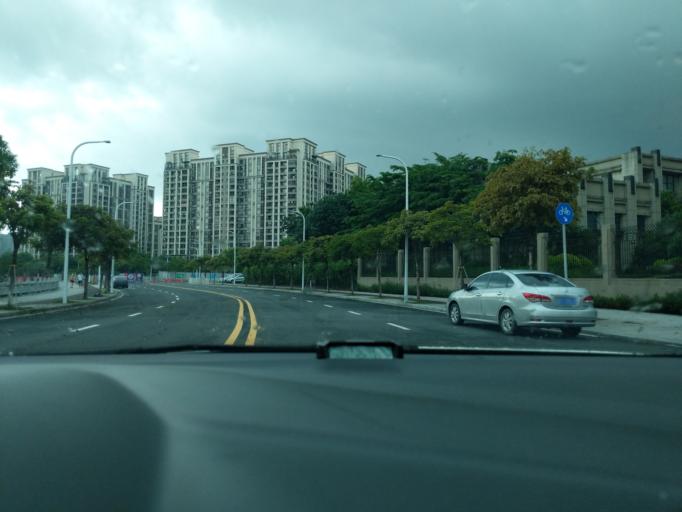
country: CN
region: Guangdong
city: Huangge
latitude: 22.7979
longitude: 113.5164
